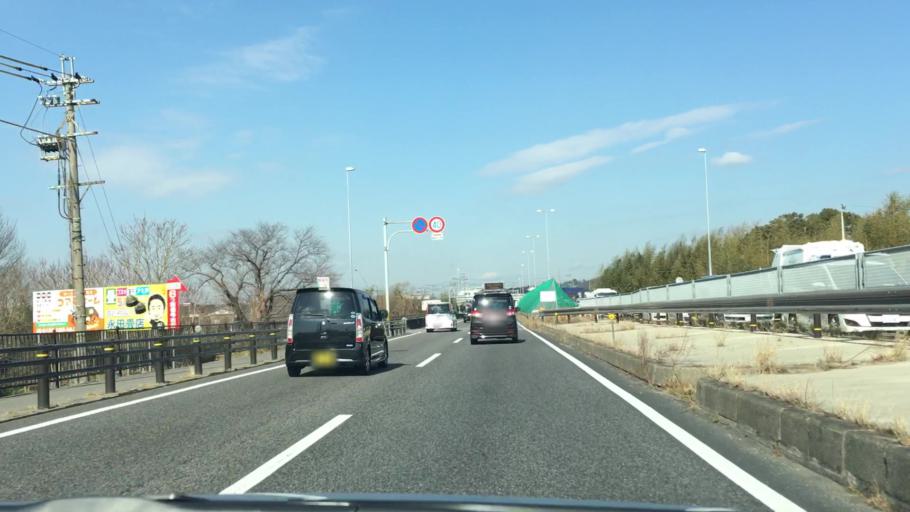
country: JP
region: Aichi
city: Okazaki
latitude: 34.9327
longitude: 137.1965
